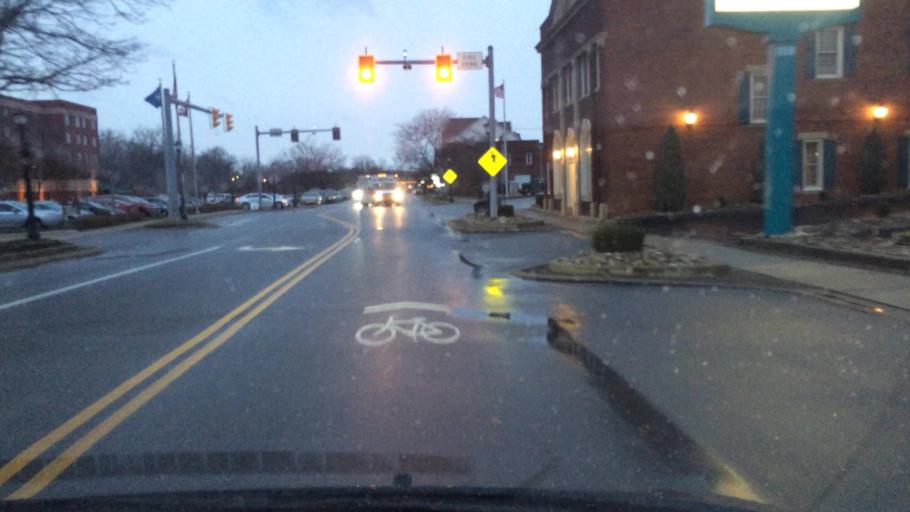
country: US
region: Ohio
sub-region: Summit County
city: Cuyahoga Falls
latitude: 41.1333
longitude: -81.4834
